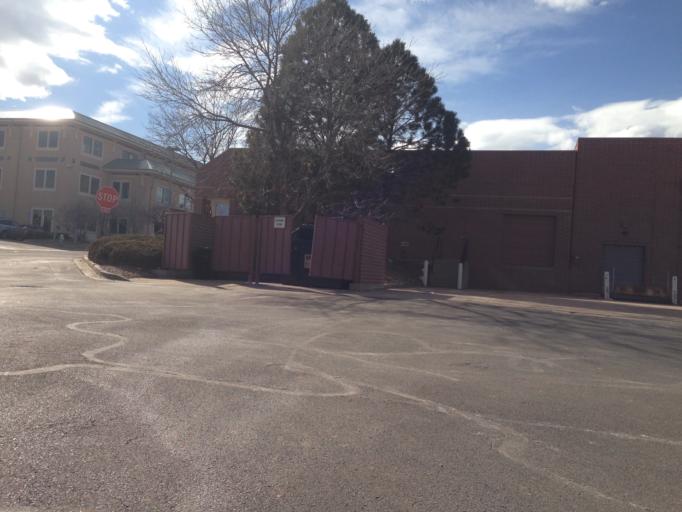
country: US
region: Colorado
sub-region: Boulder County
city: Boulder
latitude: 39.9981
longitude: -105.2352
